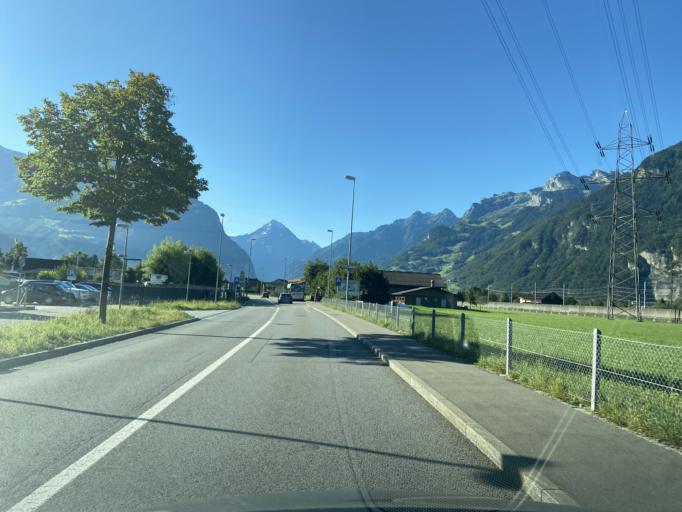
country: CH
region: Uri
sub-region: Uri
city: Flueelen
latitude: 46.8935
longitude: 8.6270
